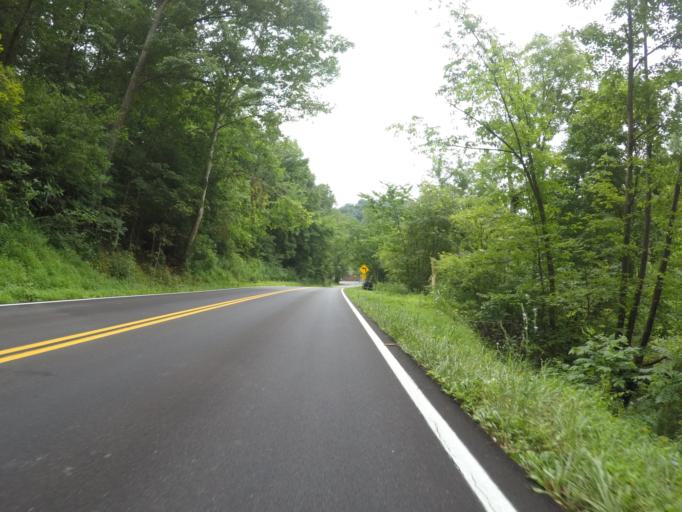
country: US
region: Kentucky
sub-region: Boyd County
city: Catlettsburg
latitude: 38.4192
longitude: -82.6214
